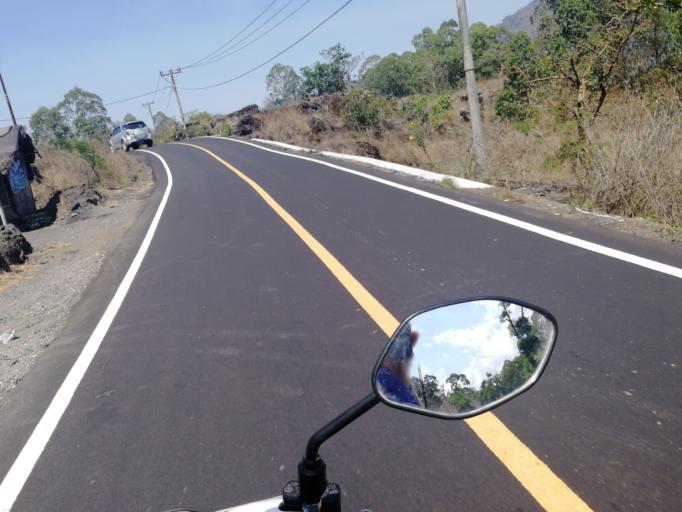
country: ID
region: Bali
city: Banjar Kedisan
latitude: -8.2616
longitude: 115.3915
